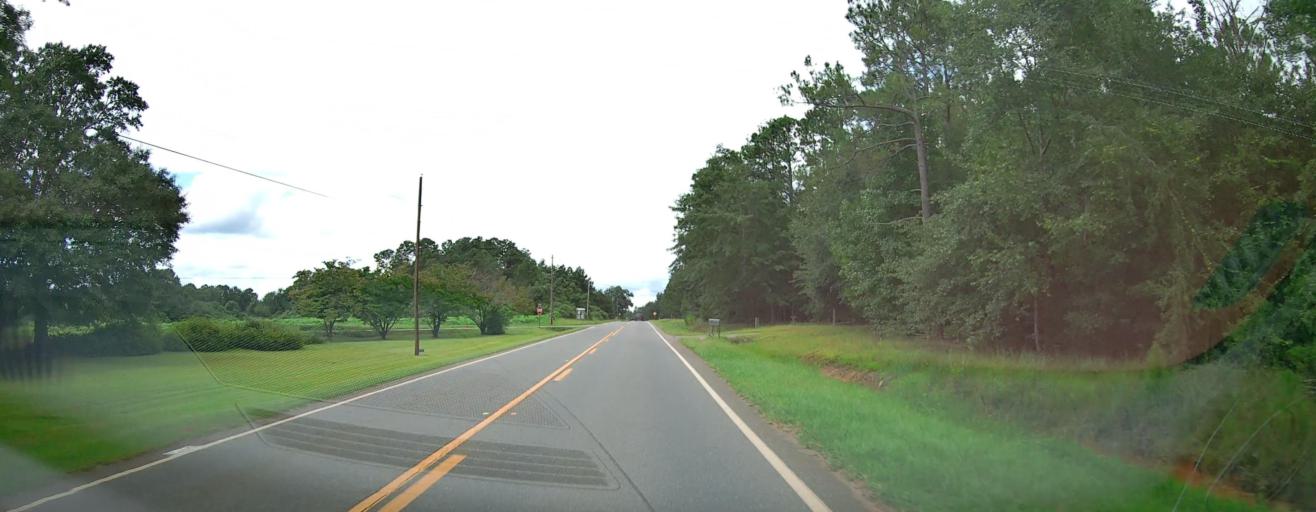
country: US
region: Georgia
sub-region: Schley County
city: Ellaville
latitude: 32.2428
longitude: -84.3187
